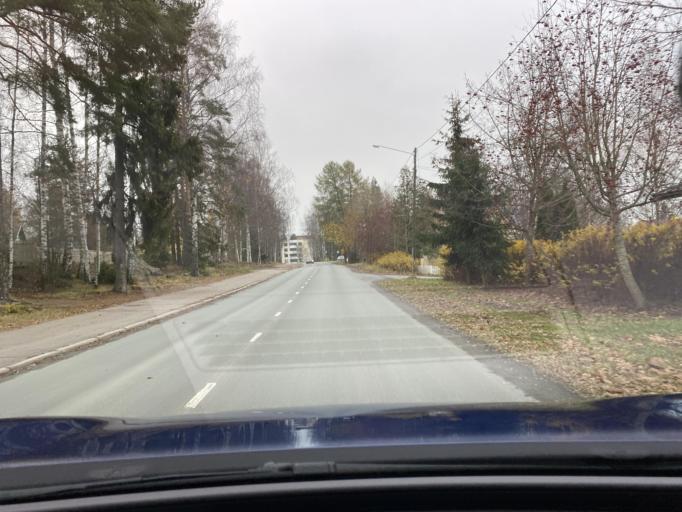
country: FI
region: Pirkanmaa
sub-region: Tampere
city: Nokia
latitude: 61.4596
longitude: 23.4949
